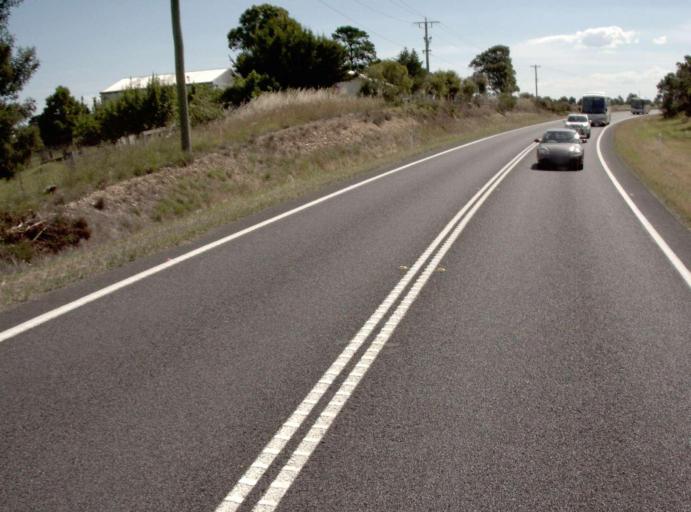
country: AU
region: Victoria
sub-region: East Gippsland
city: Bairnsdale
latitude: -37.8262
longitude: 147.7157
